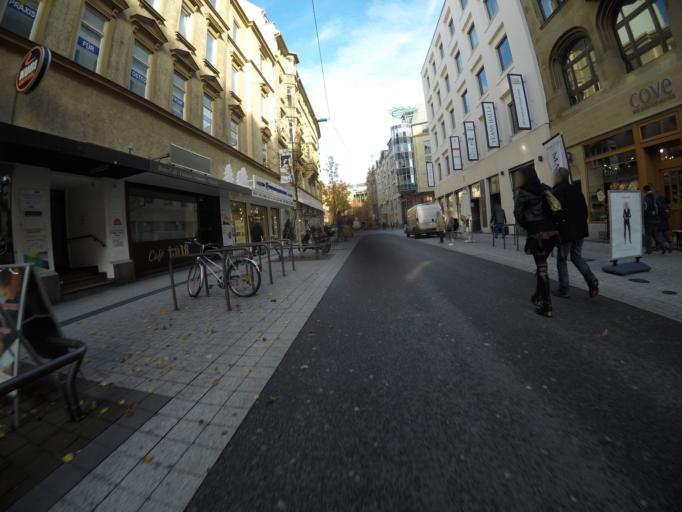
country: DE
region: Baden-Wuerttemberg
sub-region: Regierungsbezirk Stuttgart
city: Stuttgart
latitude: 48.7720
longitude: 9.1742
